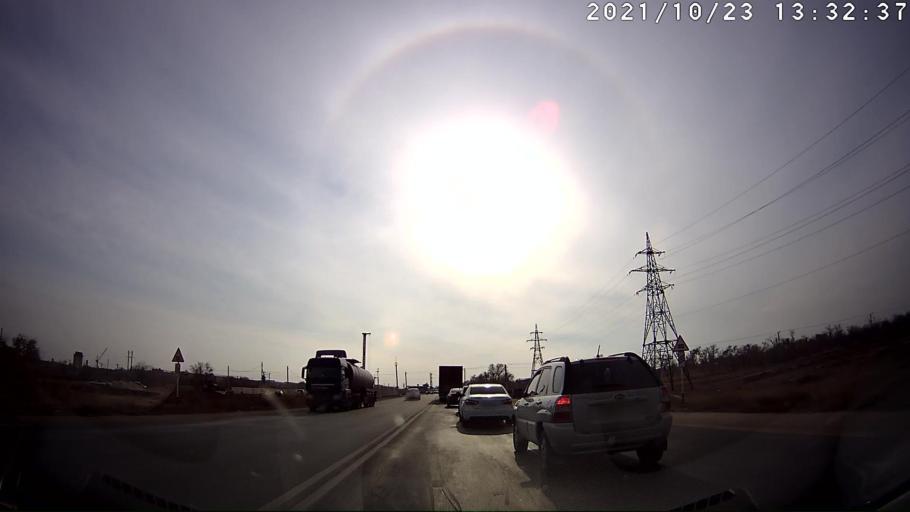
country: RU
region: Volgograd
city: Vodstroy
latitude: 48.8619
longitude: 44.5648
